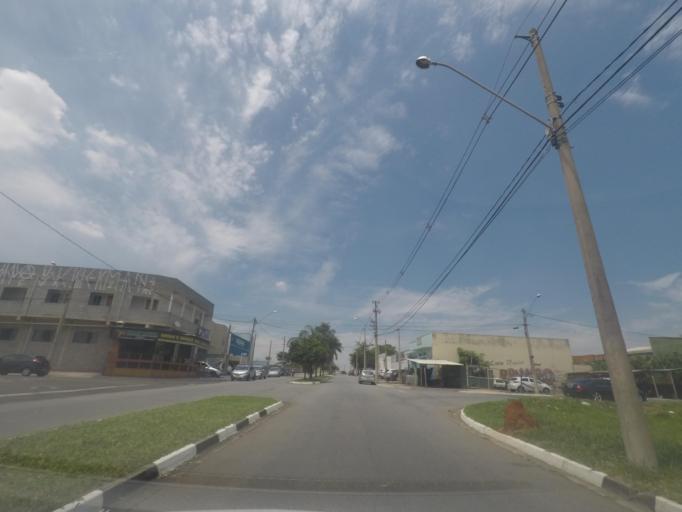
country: BR
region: Sao Paulo
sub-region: Sumare
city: Sumare
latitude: -22.8004
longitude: -47.2725
